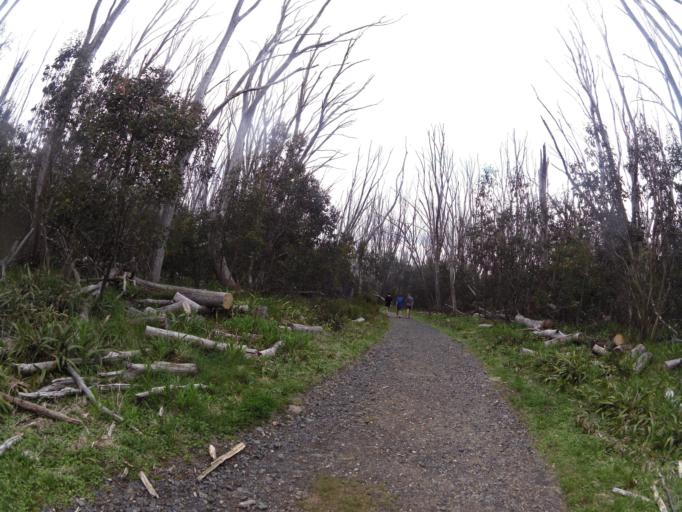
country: AU
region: Victoria
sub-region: Yarra Ranges
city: Millgrove
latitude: -37.5004
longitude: 145.8787
